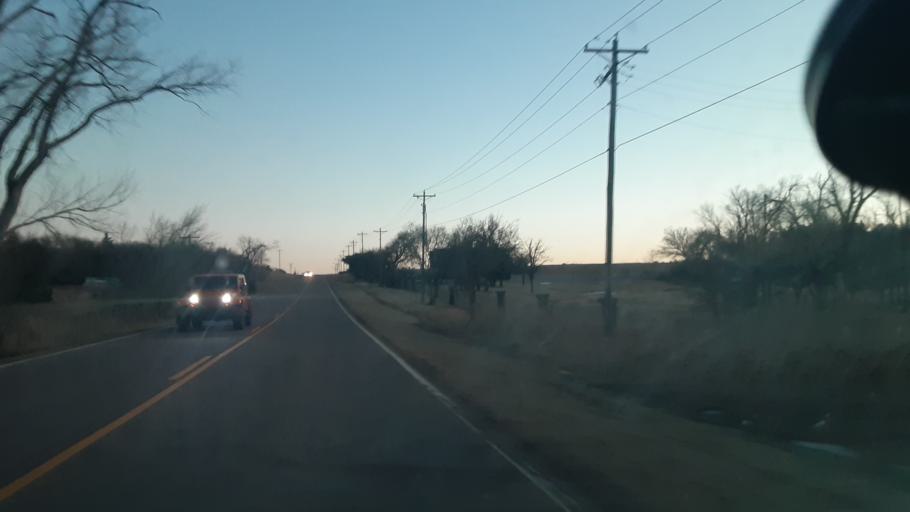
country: US
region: Oklahoma
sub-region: Oklahoma County
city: Edmond
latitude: 35.6891
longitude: -97.4251
